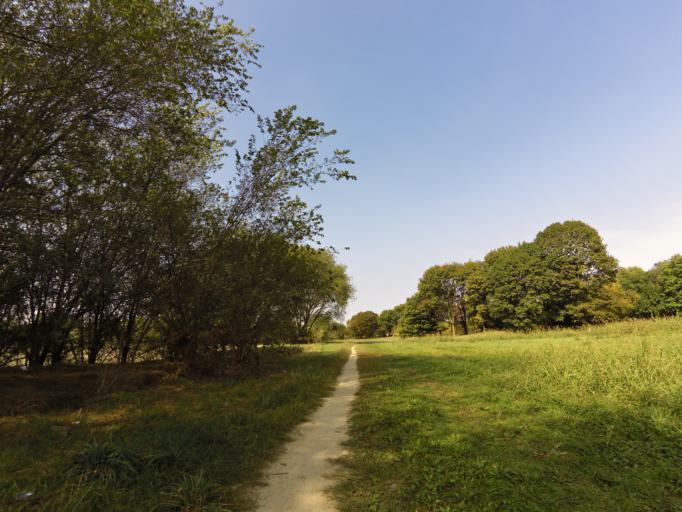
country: IT
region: Lombardy
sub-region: Citta metropolitana di Milano
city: Chiaravalle
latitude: 45.4310
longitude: 9.2356
